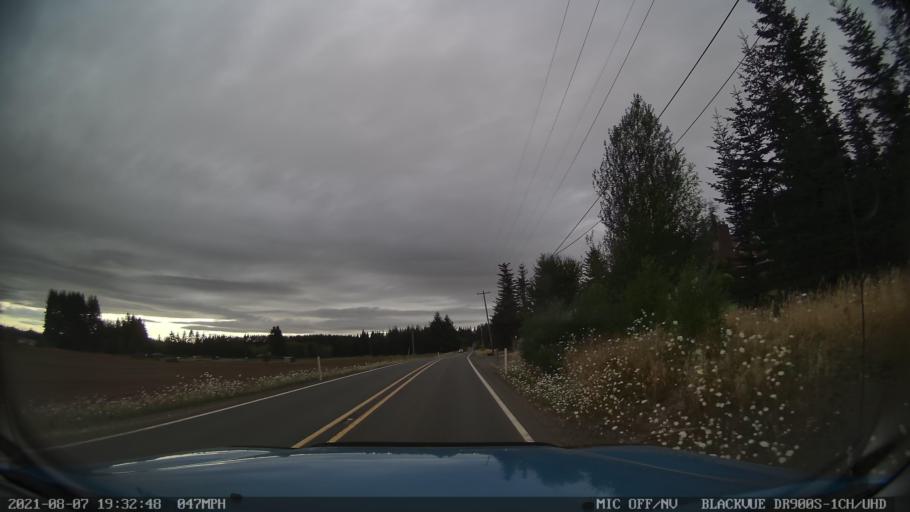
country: US
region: Oregon
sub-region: Linn County
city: Lyons
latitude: 44.9028
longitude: -122.6481
